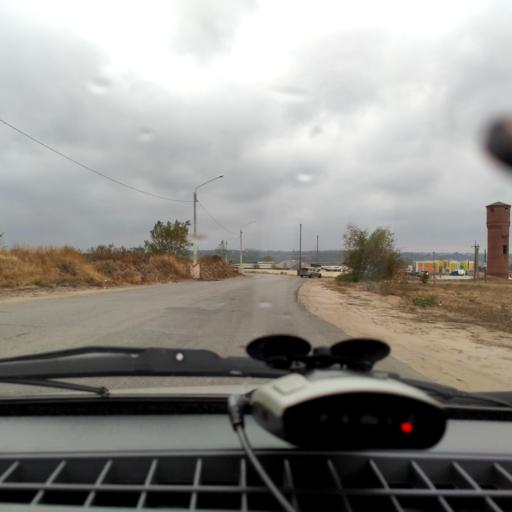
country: RU
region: Voronezj
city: Pridonskoy
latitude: 51.6984
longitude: 39.0766
